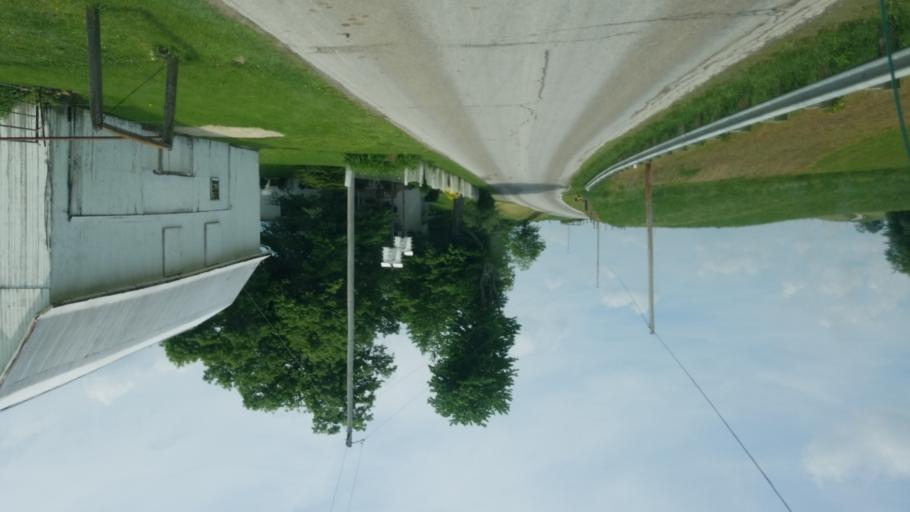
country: US
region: Ohio
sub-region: Tuscarawas County
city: Sugarcreek
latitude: 40.4543
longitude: -81.7922
